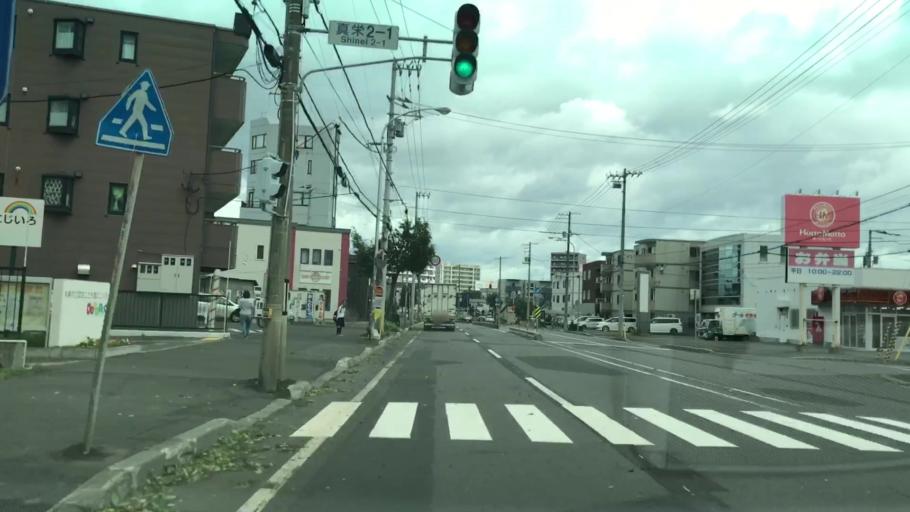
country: JP
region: Hokkaido
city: Sapporo
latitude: 42.9935
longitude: 141.4409
